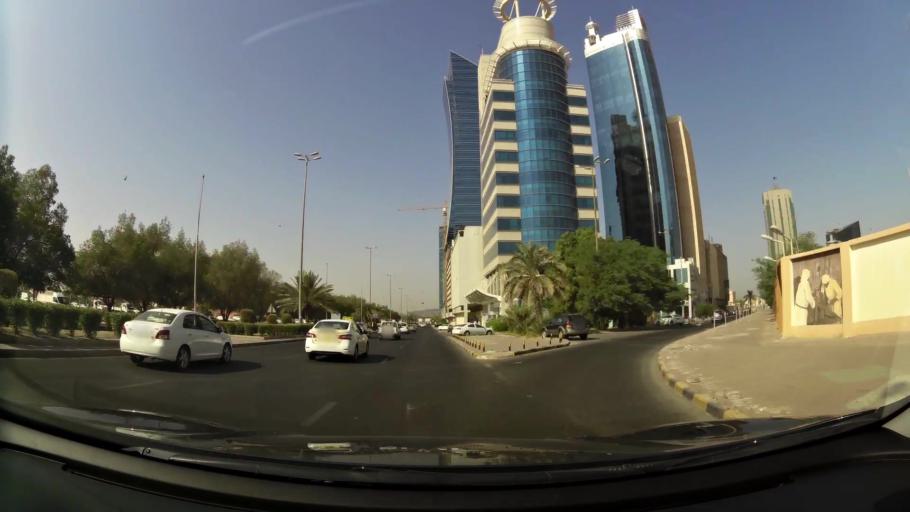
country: KW
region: Al Asimah
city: Kuwait City
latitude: 29.3612
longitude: 47.9692
